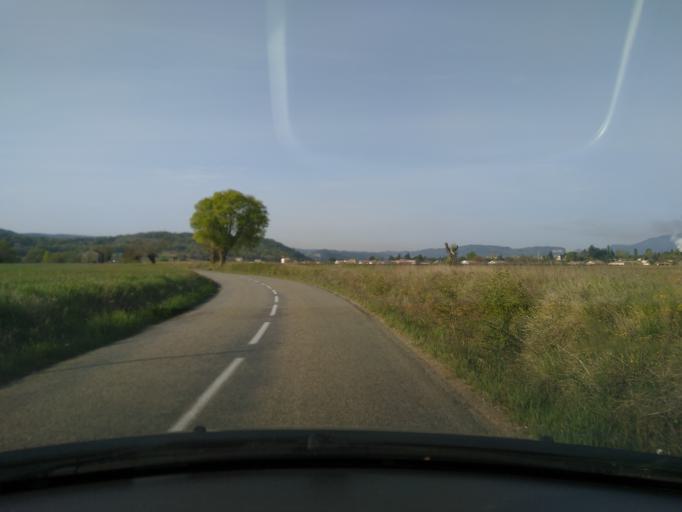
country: FR
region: Rhone-Alpes
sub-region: Departement de l'Ardeche
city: Ruoms
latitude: 44.4161
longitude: 4.4094
